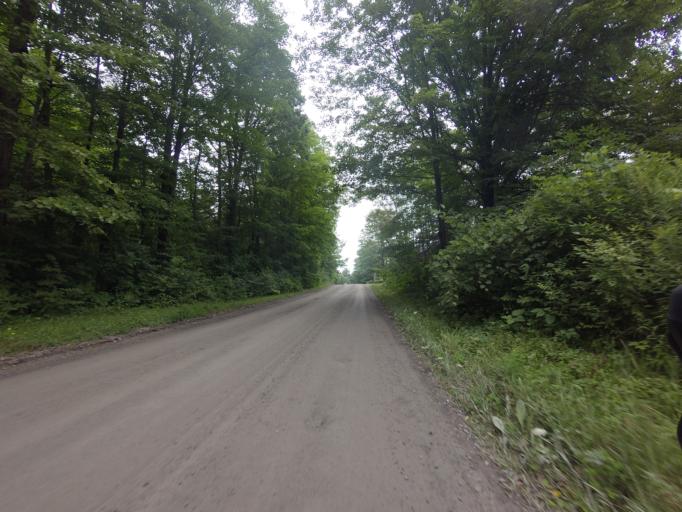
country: CA
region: Ontario
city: Kingston
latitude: 44.5582
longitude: -76.6275
